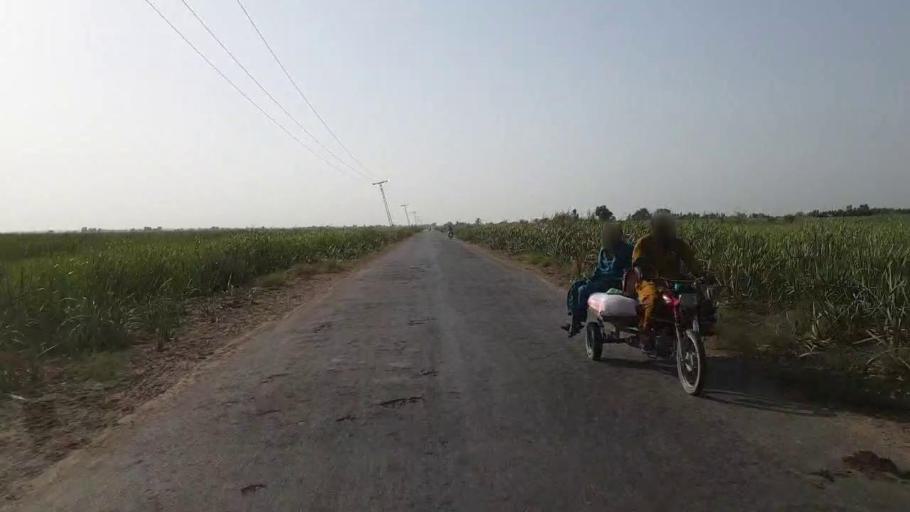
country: PK
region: Sindh
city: Jam Sahib
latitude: 26.4101
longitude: 68.8754
